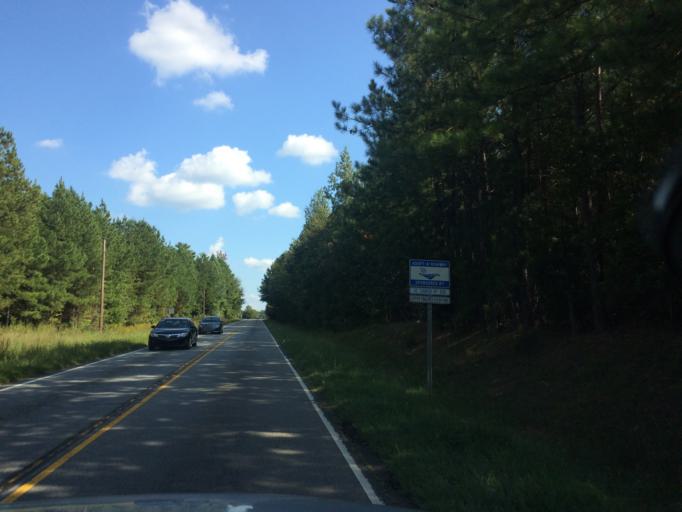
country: US
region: South Carolina
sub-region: Greenville County
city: Fountain Inn
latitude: 34.6390
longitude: -82.1440
